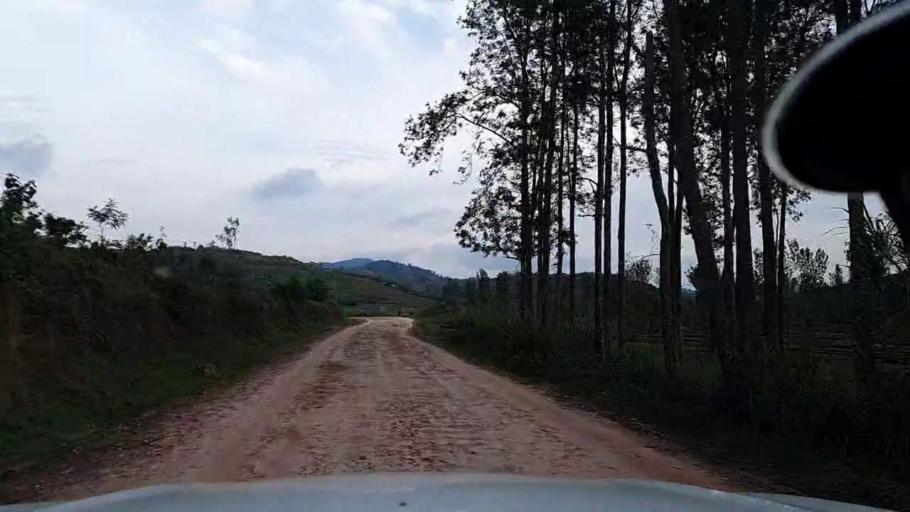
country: RW
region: Southern Province
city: Nyanza
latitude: -2.2127
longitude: 29.6187
